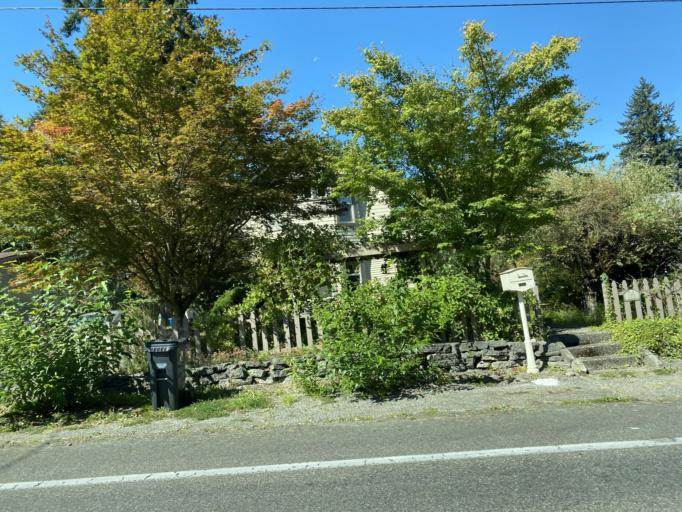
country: US
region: Washington
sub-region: Thurston County
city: Olympia
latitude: 47.0333
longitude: -122.8868
